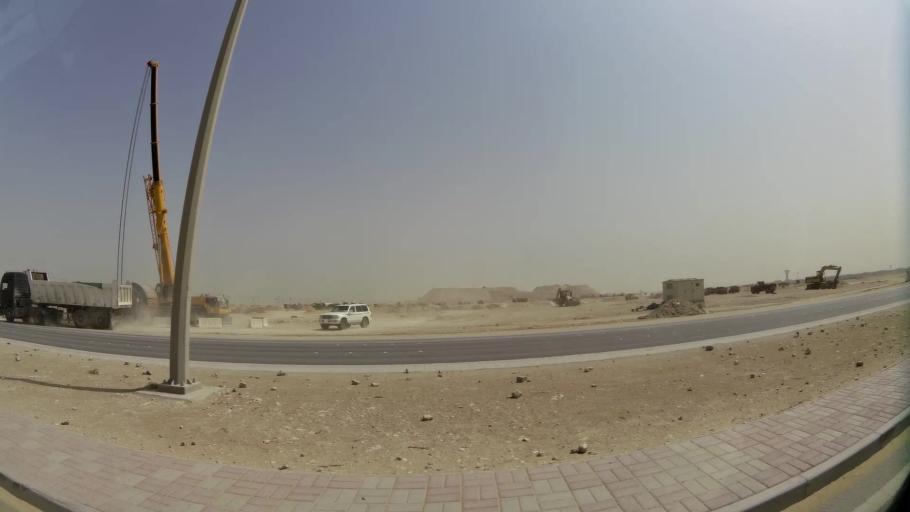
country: QA
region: Baladiyat ar Rayyan
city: Ar Rayyan
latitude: 25.1742
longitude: 51.3996
